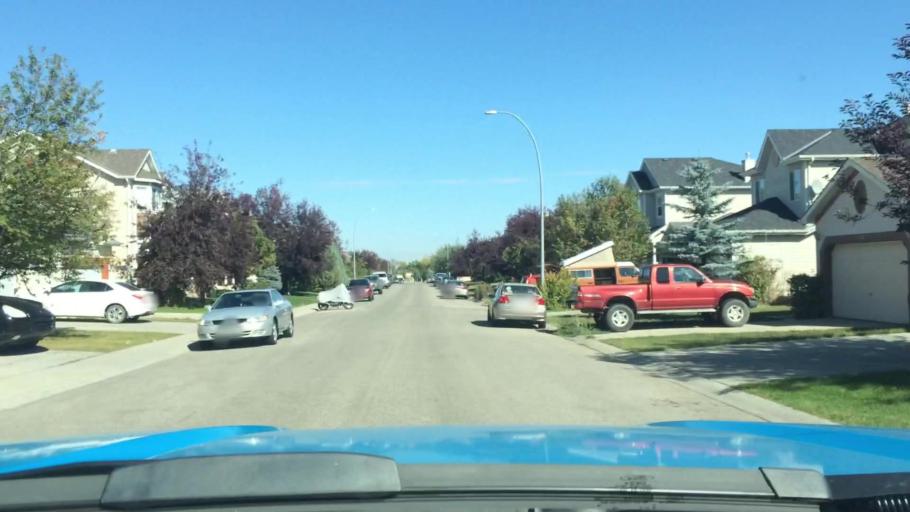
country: CA
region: Alberta
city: Calgary
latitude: 50.9043
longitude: -114.1091
